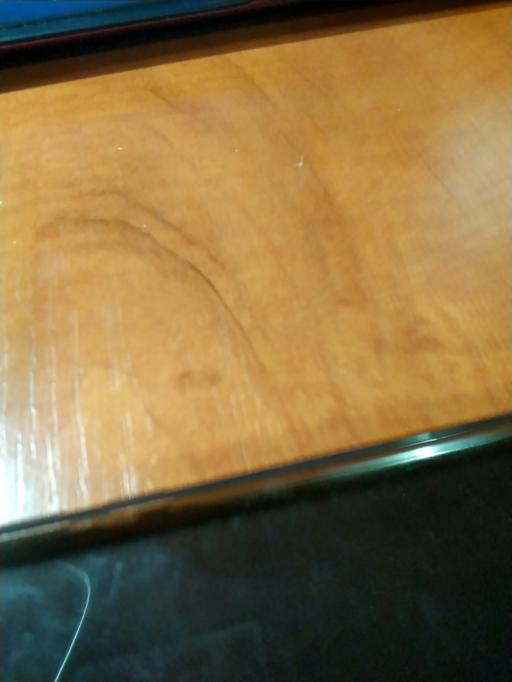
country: RU
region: Kaluga
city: Iznoski
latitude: 54.8839
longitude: 35.3631
